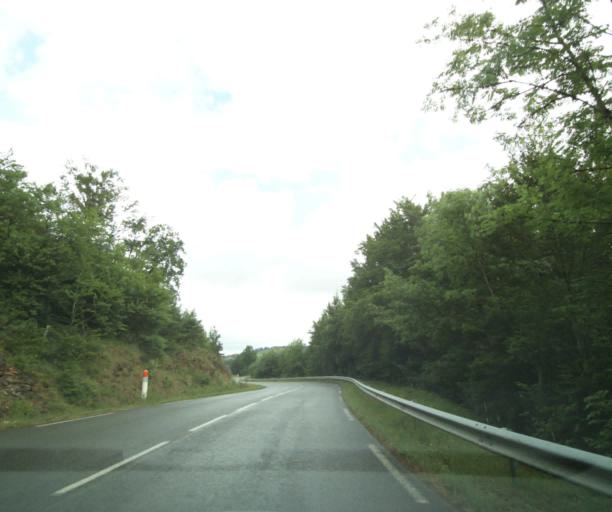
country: FR
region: Languedoc-Roussillon
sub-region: Departement de la Lozere
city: La Canourgue
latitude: 44.4008
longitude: 3.1410
